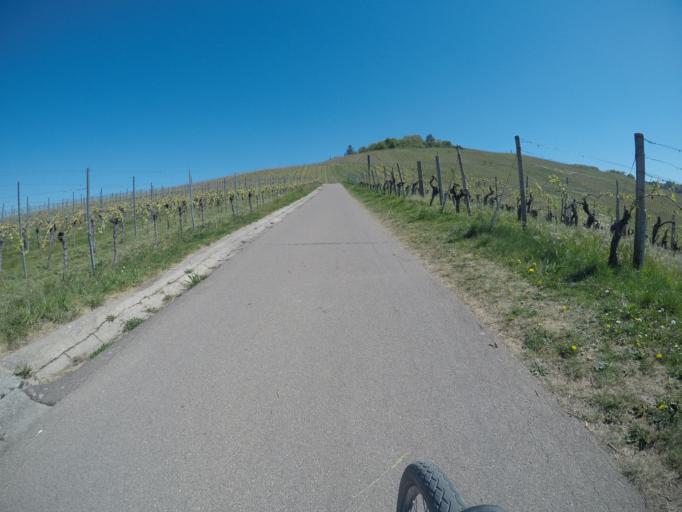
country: DE
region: Baden-Wuerttemberg
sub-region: Regierungsbezirk Stuttgart
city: Fellbach
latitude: 48.7963
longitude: 9.2727
